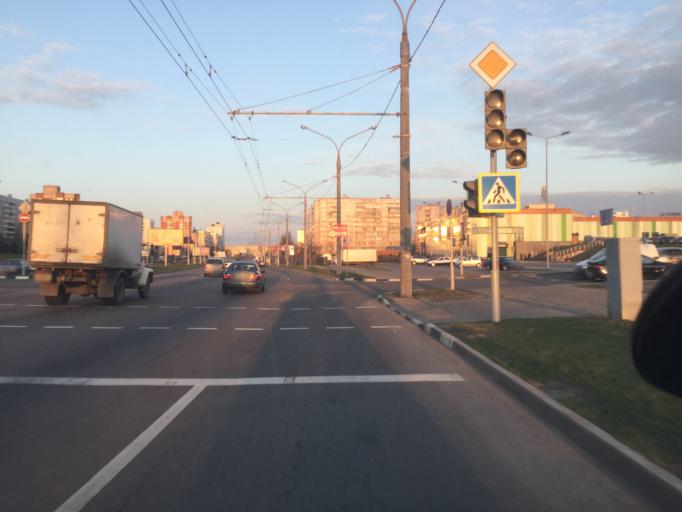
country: BY
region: Vitebsk
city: Vitebsk
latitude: 55.1639
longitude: 30.2051
